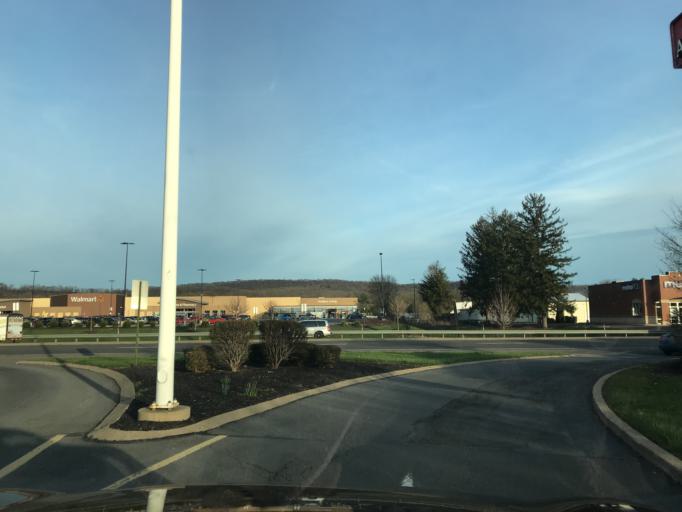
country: US
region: Pennsylvania
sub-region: Snyder County
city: Hummels Wharf
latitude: 40.8239
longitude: -76.8480
